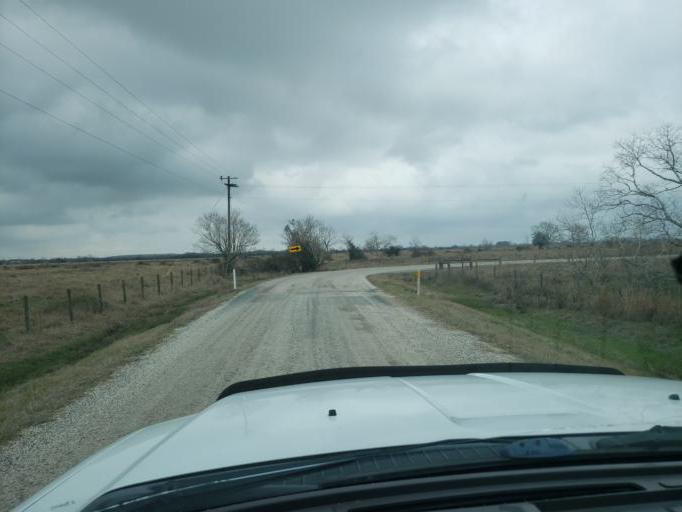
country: US
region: Texas
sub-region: Fort Bend County
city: Needville
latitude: 29.3637
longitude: -95.7392
